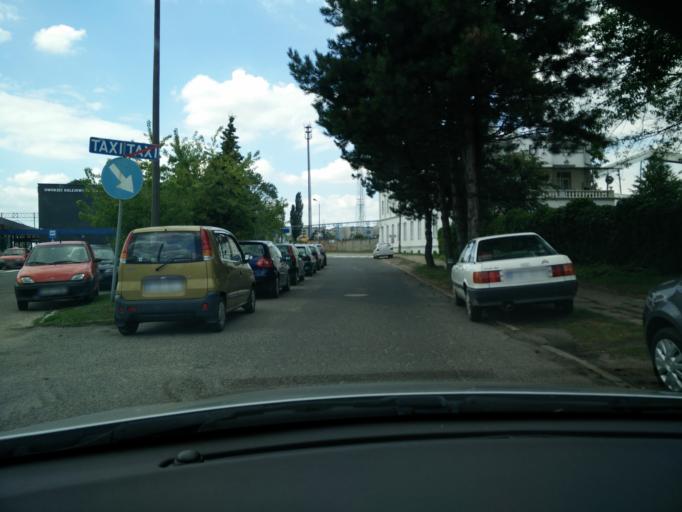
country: PL
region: Greater Poland Voivodeship
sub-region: Powiat sredzki
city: Sroda Wielkopolska
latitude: 52.2176
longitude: 17.2762
